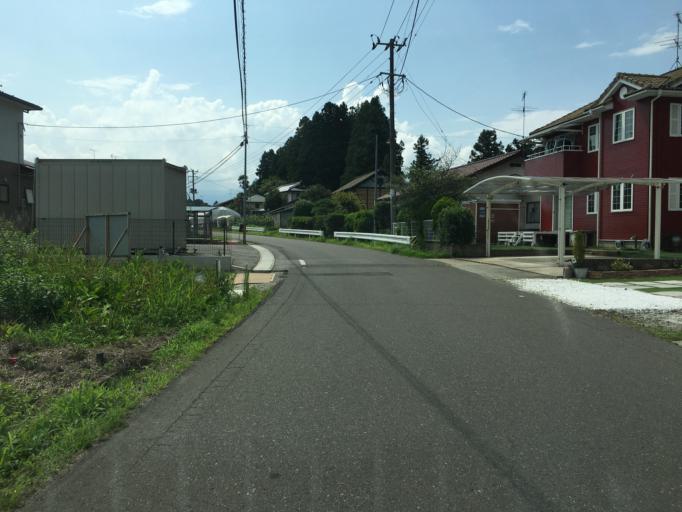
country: JP
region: Fukushima
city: Nihommatsu
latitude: 37.6245
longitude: 140.4551
